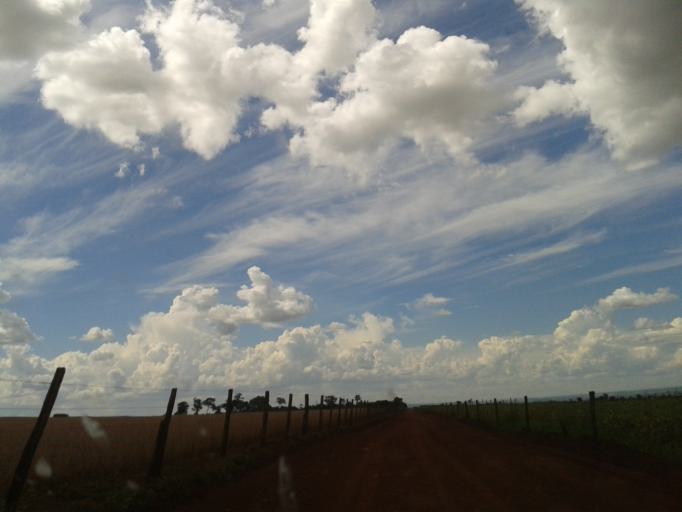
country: BR
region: Minas Gerais
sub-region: Capinopolis
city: Capinopolis
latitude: -18.7183
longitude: -49.7705
